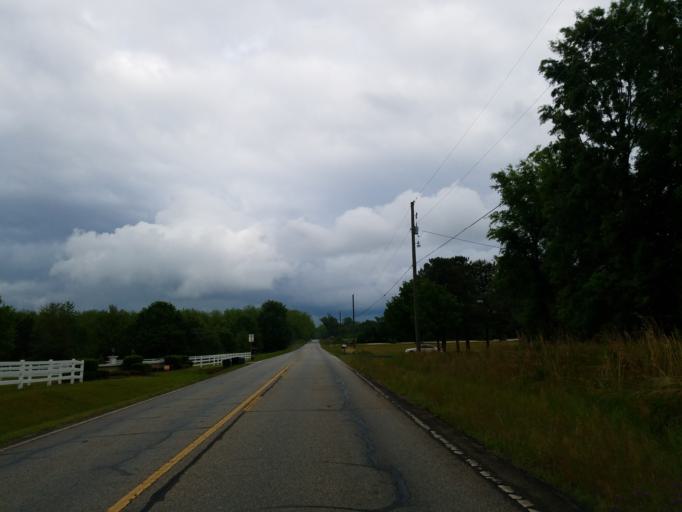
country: US
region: Georgia
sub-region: Peach County
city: Byron
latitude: 32.6517
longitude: -83.7844
